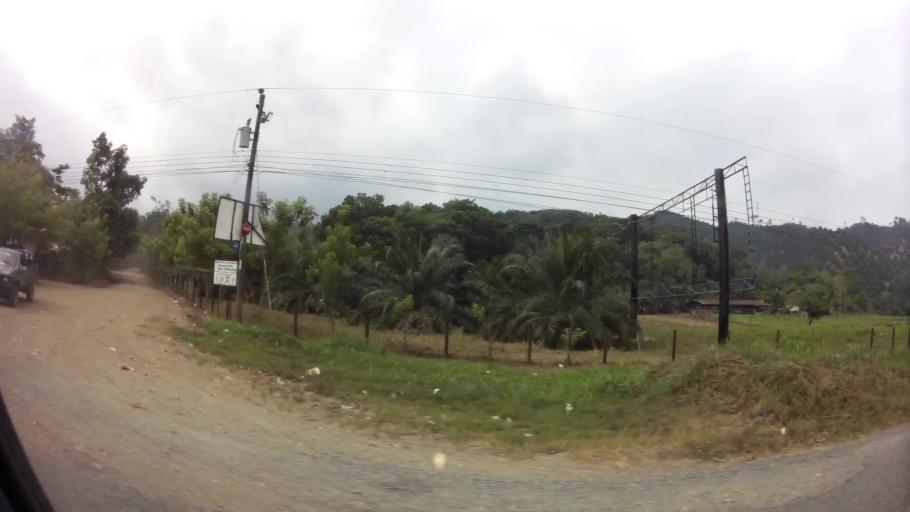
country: HN
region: Yoro
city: Guaimitas
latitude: 15.4943
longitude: -87.7324
